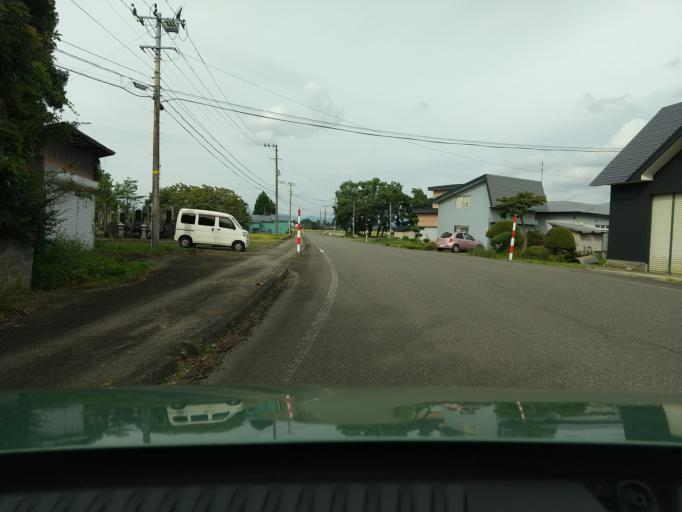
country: JP
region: Akita
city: Kakunodatemachi
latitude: 39.5504
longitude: 140.5678
